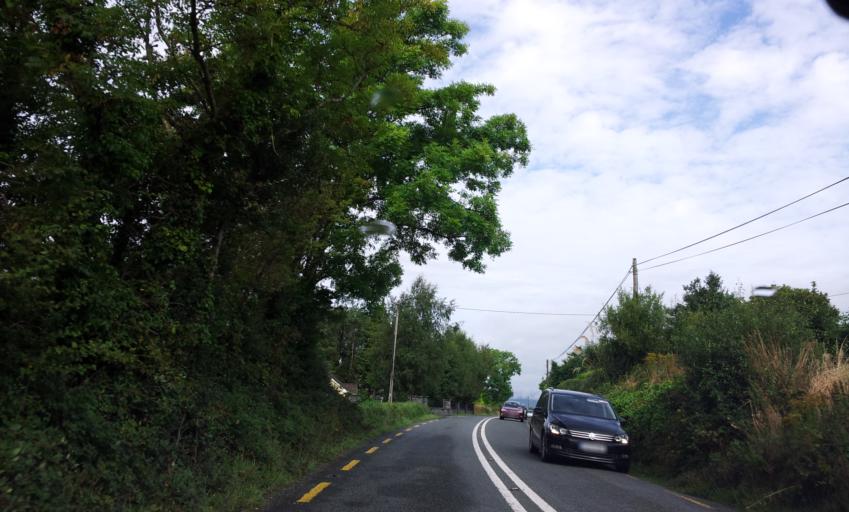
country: IE
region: Munster
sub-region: Ciarrai
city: Killorglin
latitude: 52.0777
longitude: -9.6585
